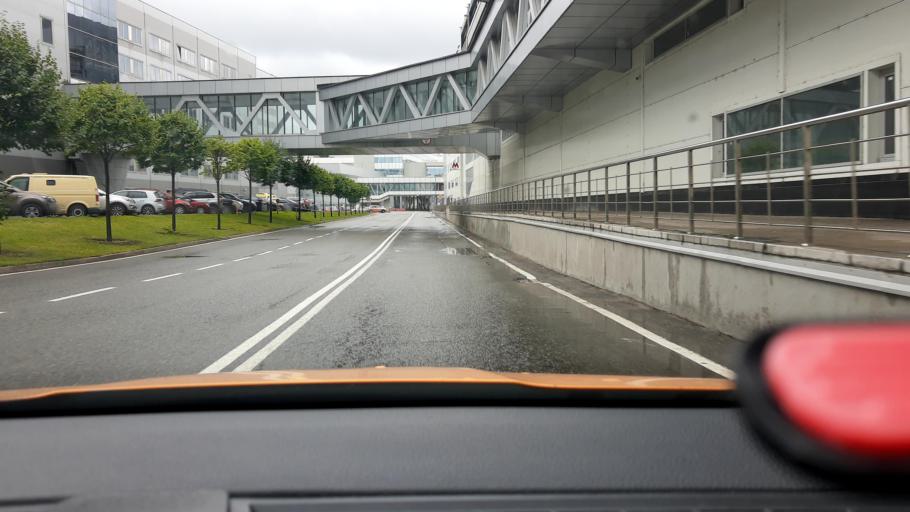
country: RU
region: Moscow
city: Strogino
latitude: 55.8255
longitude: 37.3855
